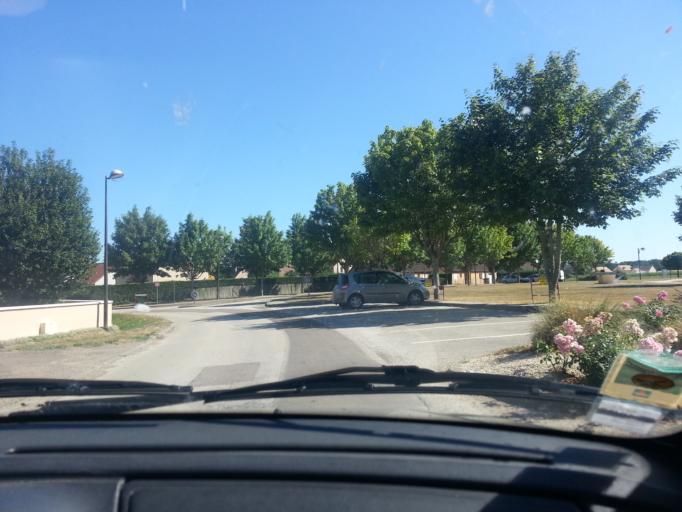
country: FR
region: Bourgogne
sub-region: Departement de Saone-et-Loire
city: Sassenay
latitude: 46.8192
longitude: 4.9681
